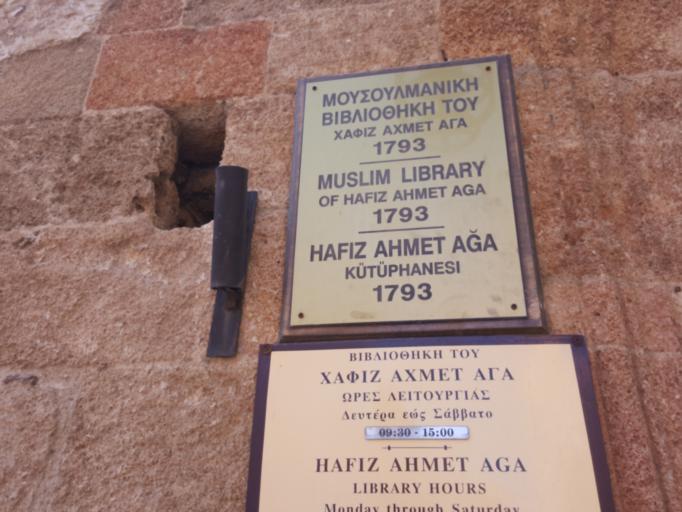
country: GR
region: South Aegean
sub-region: Nomos Dodekanisou
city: Rodos
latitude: 36.4439
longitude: 28.2239
